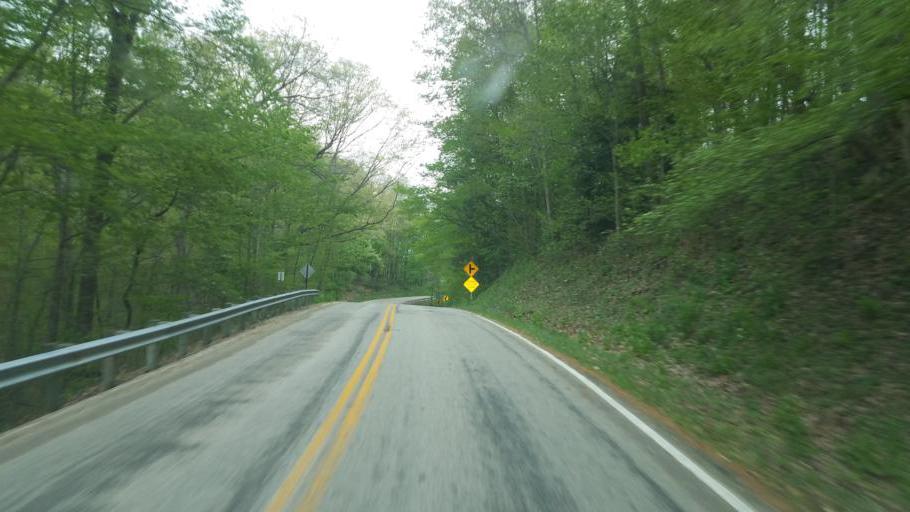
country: US
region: Ohio
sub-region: Ashland County
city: Loudonville
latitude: 40.6410
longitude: -82.3239
